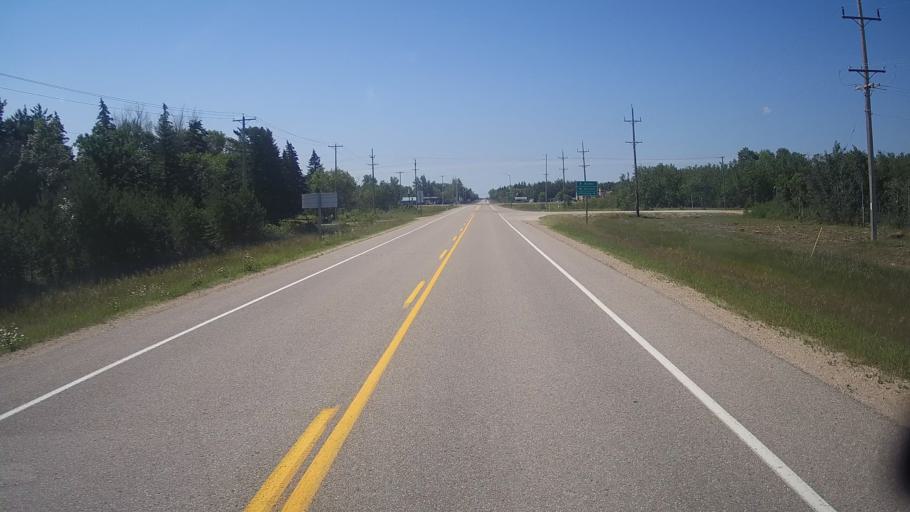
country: CA
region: Manitoba
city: La Broquerie
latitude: 49.6663
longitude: -96.4568
